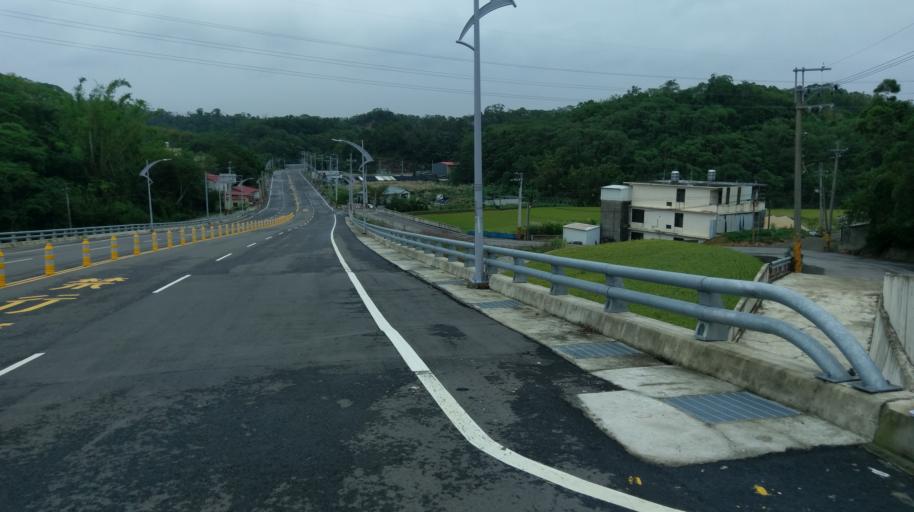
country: TW
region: Taiwan
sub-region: Hsinchu
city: Hsinchu
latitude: 24.7428
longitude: 120.9605
